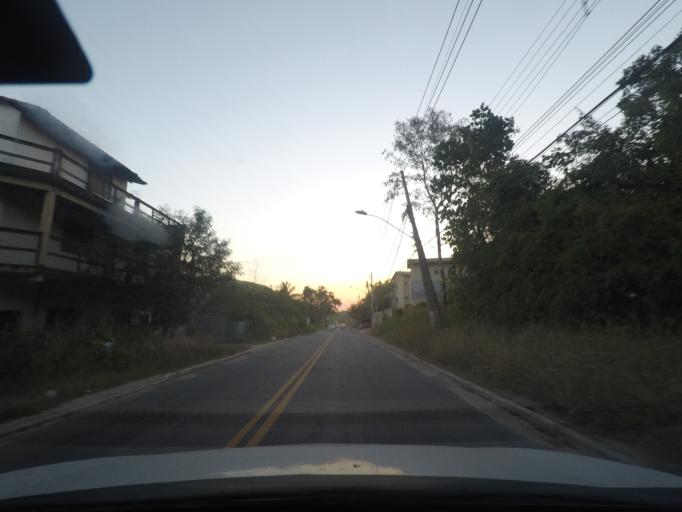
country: BR
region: Rio de Janeiro
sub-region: Marica
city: Marica
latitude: -22.9456
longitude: -42.9636
